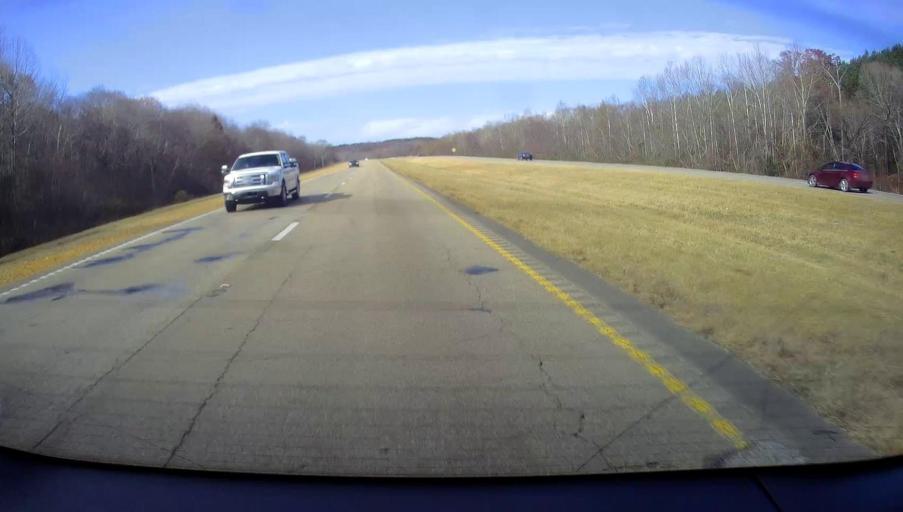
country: US
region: Mississippi
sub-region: Alcorn County
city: Corinth
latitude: 34.9407
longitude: -88.7810
